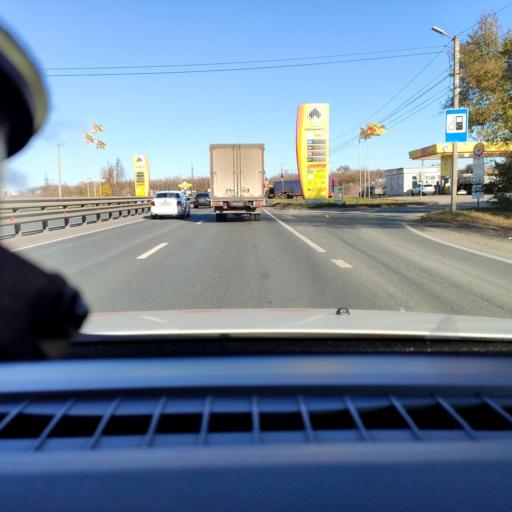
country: RU
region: Samara
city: Samara
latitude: 53.1236
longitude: 50.1701
